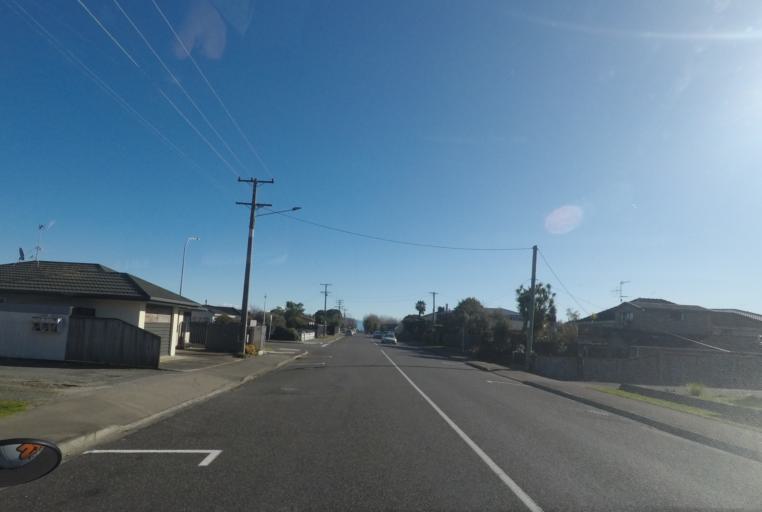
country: NZ
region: Nelson
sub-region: Nelson City
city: Nelson
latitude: -41.2875
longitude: 173.2370
